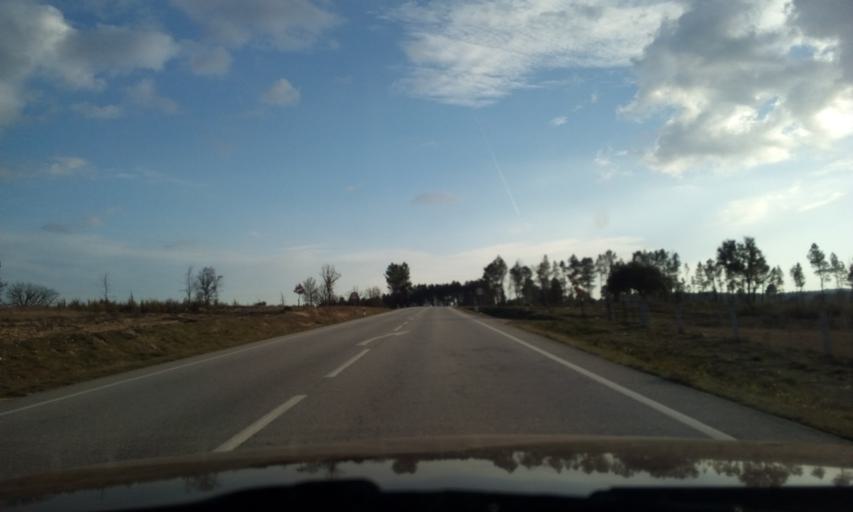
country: PT
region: Guarda
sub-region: Pinhel
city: Pinhel
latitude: 40.6457
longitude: -6.9683
